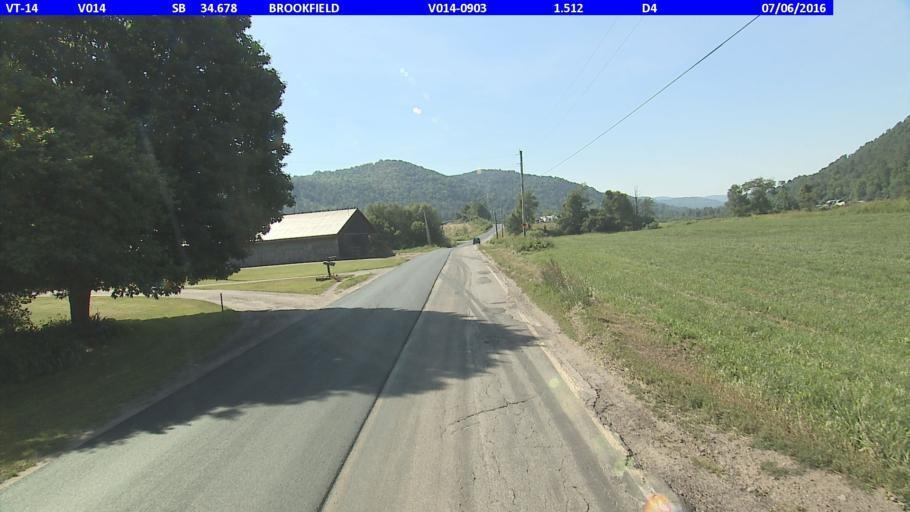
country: US
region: Vermont
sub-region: Orange County
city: Chelsea
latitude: 44.0001
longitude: -72.5609
